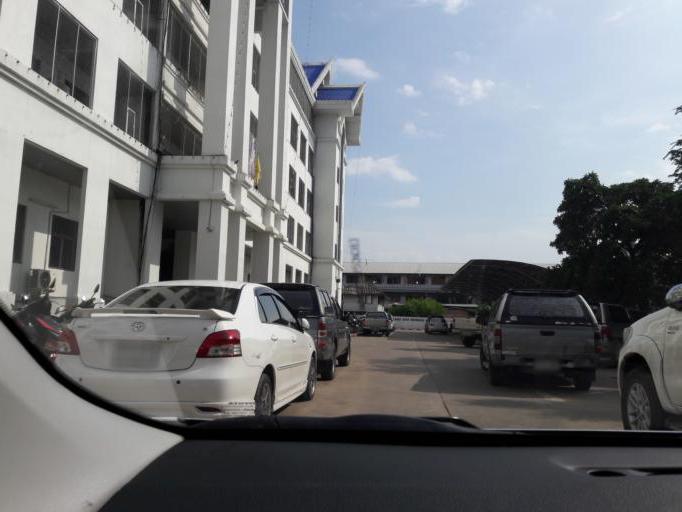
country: TH
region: Ang Thong
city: Ang Thong
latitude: 14.5885
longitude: 100.4546
